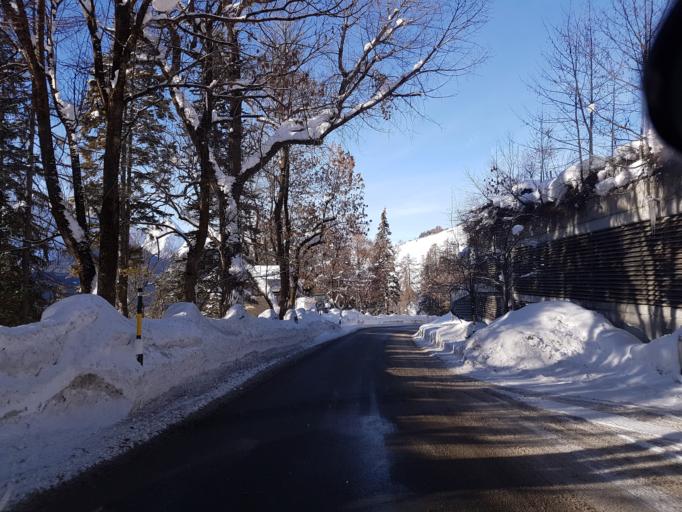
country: CH
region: Grisons
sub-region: Inn District
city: Scuol
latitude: 46.8160
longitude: 10.3322
